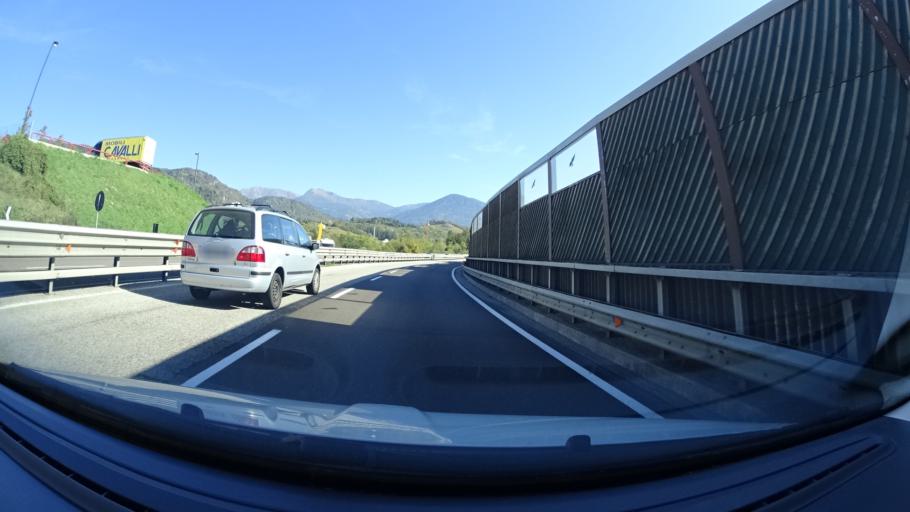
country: IT
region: Trentino-Alto Adige
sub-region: Provincia di Trento
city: Civezzano
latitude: 46.0817
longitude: 11.1968
